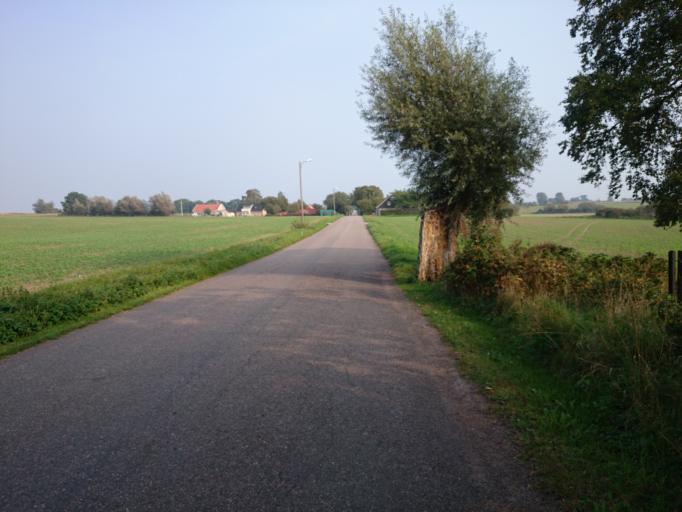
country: SE
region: Skane
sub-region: Helsingborg
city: Rydeback
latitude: 55.9054
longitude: 12.7060
